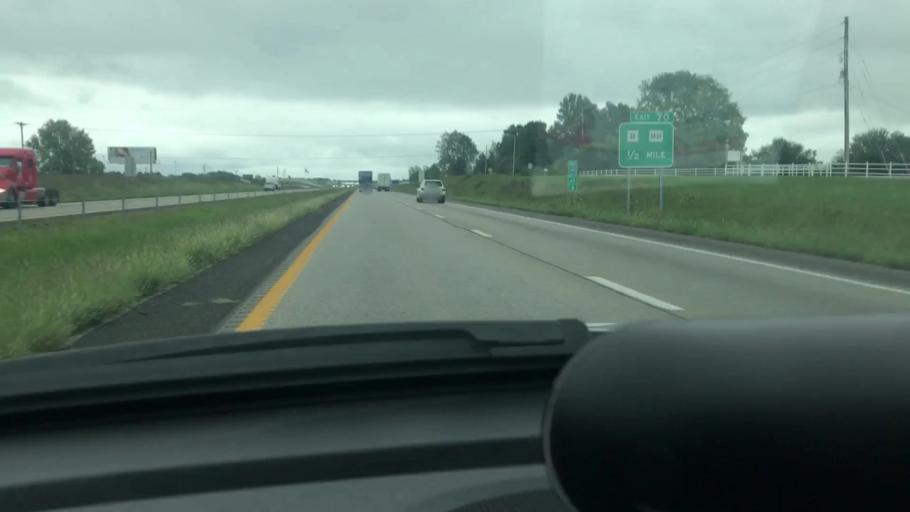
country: US
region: Missouri
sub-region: Greene County
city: Republic
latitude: 37.1982
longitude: -93.4341
